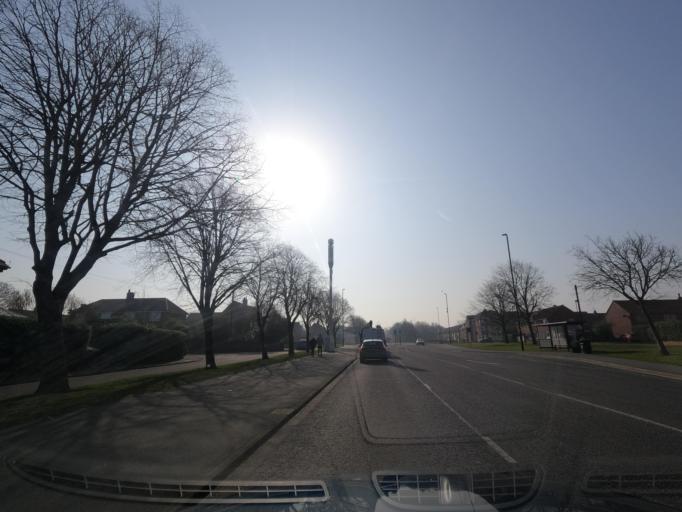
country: GB
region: England
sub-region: Newcastle upon Tyne
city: Gosforth
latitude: 55.0138
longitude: -1.5824
